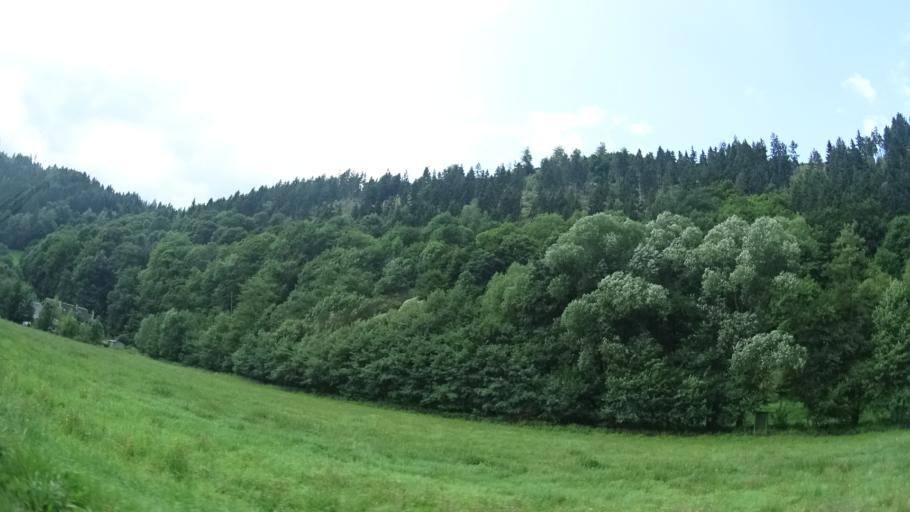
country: DE
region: Thuringia
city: Probstzella
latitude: 50.5488
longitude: 11.3483
